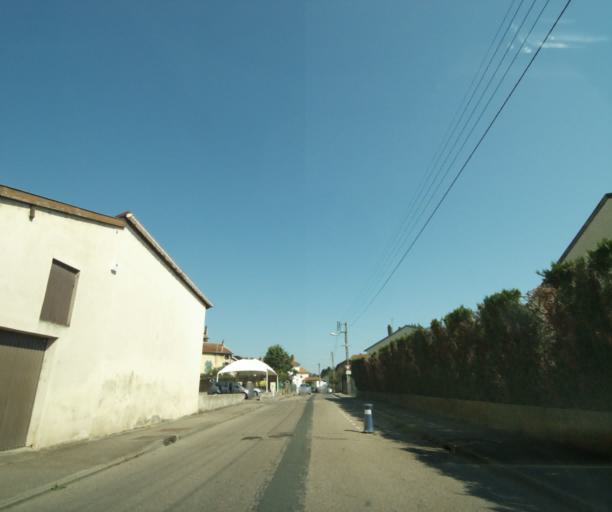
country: FR
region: Lorraine
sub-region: Departement de Meurthe-et-Moselle
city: Toul
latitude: 48.6674
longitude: 5.8830
